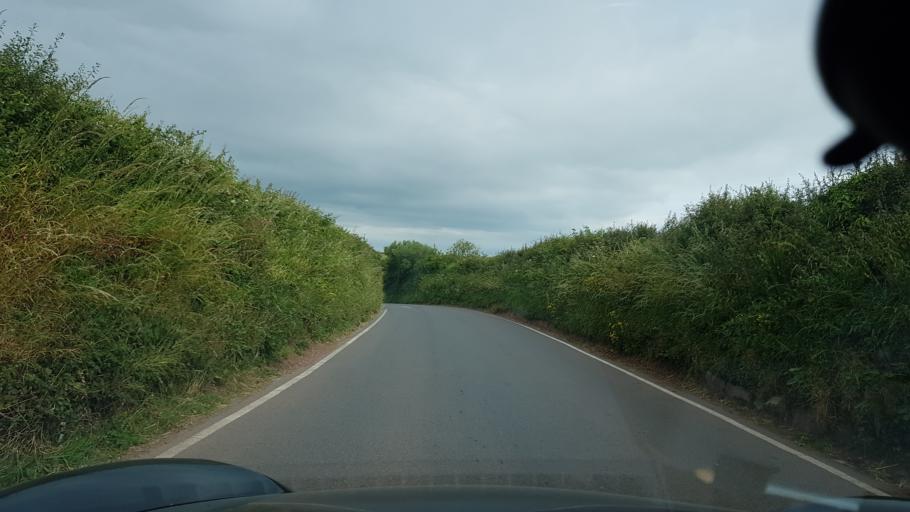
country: GB
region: Wales
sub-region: Pembrokeshire
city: Dale
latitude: 51.7499
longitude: -5.1376
